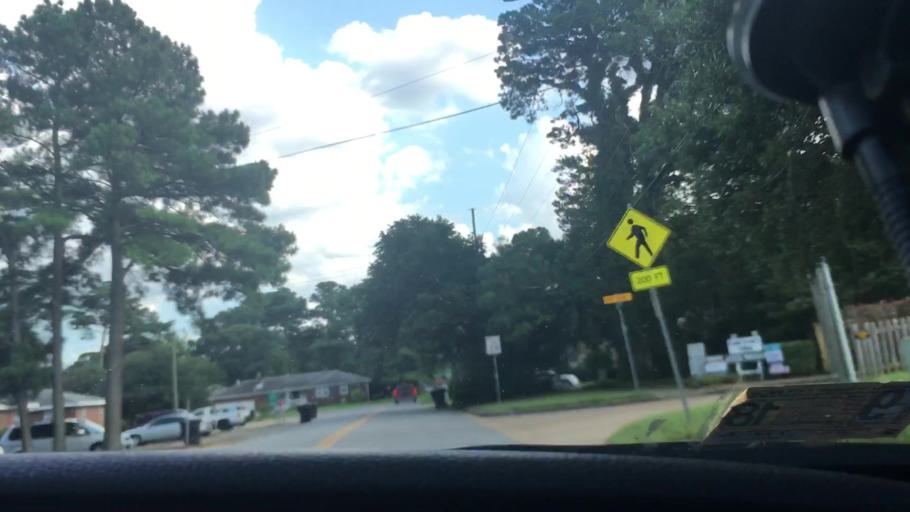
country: US
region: Virginia
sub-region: City of Virginia Beach
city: Virginia Beach
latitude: 36.9099
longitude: -76.0776
